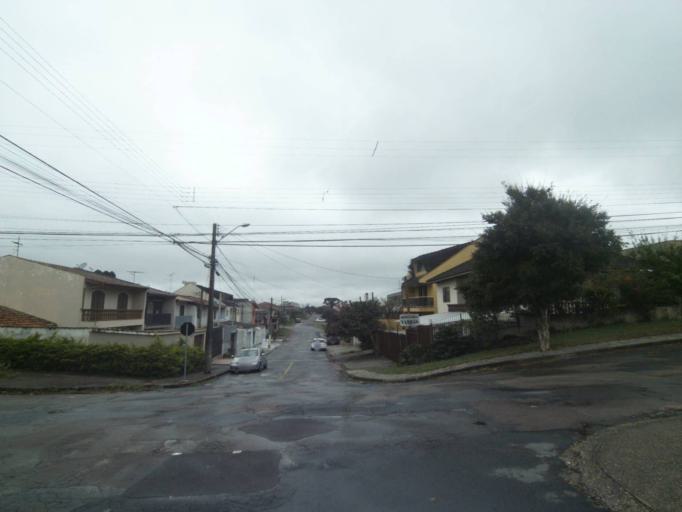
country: BR
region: Parana
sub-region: Curitiba
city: Curitiba
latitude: -25.5015
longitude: -49.3058
